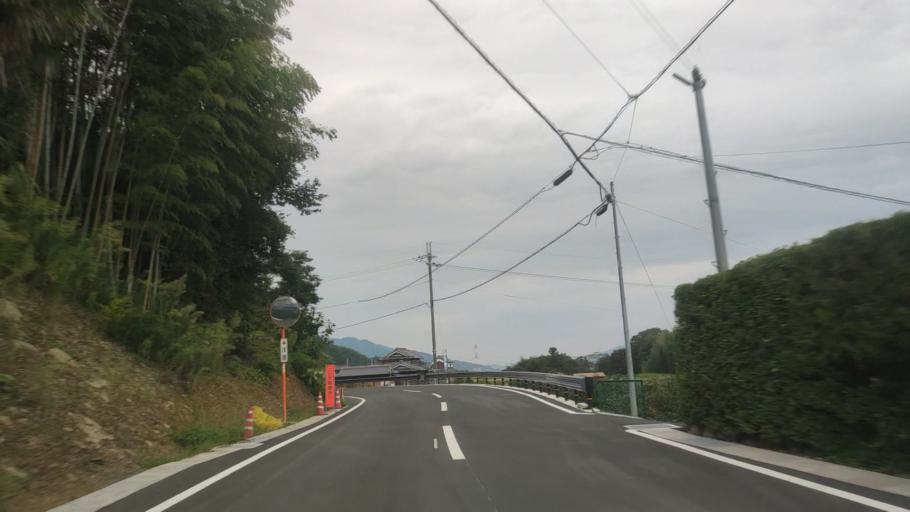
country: JP
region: Wakayama
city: Hashimoto
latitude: 34.3108
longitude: 135.6183
